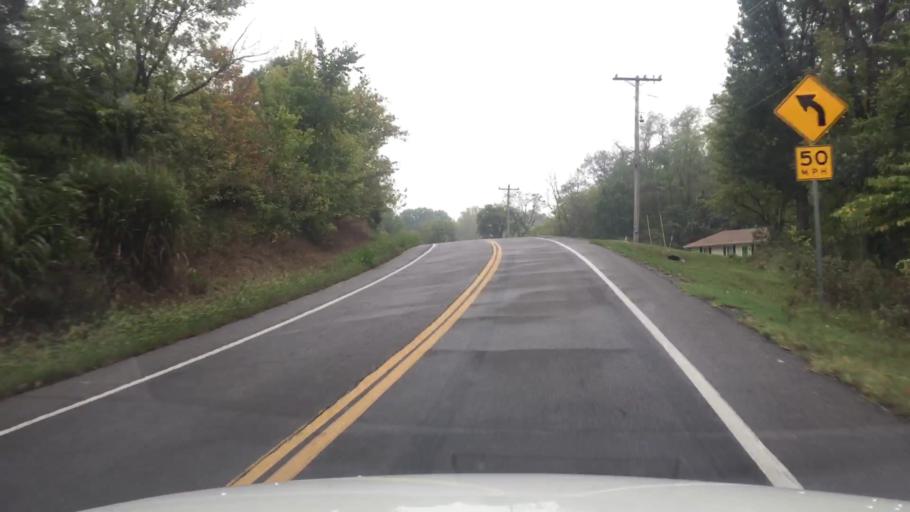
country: US
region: Missouri
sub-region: Boone County
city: Columbia
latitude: 38.8791
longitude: -92.4191
